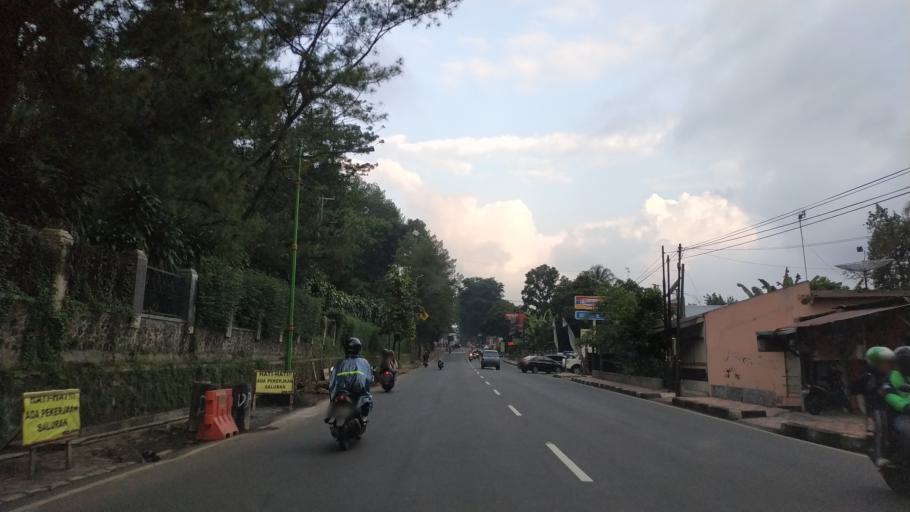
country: ID
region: Central Java
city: Salatiga
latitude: -7.3135
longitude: 110.4923
